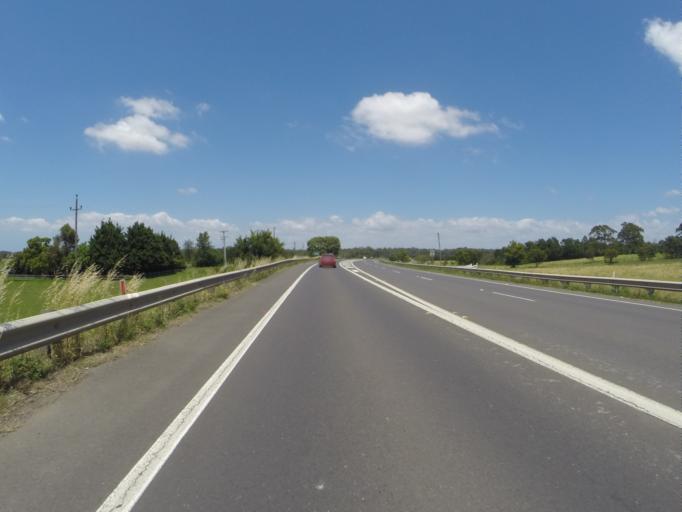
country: AU
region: New South Wales
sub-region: Shoalhaven Shire
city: Bomaderry
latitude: -34.8211
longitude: 150.6063
